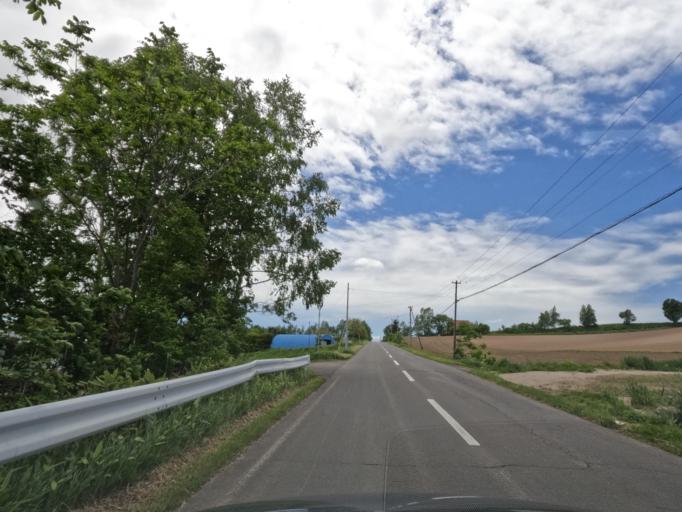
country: JP
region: Hokkaido
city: Shimo-furano
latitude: 43.5240
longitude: 142.4335
